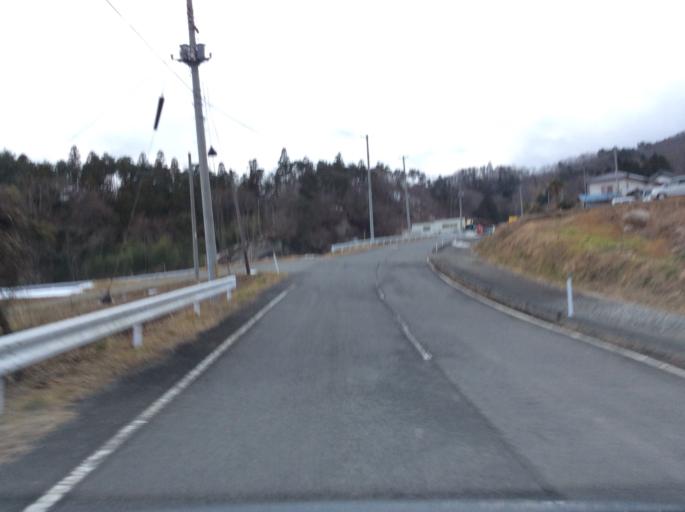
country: JP
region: Fukushima
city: Iwaki
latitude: 37.1737
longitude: 140.9434
